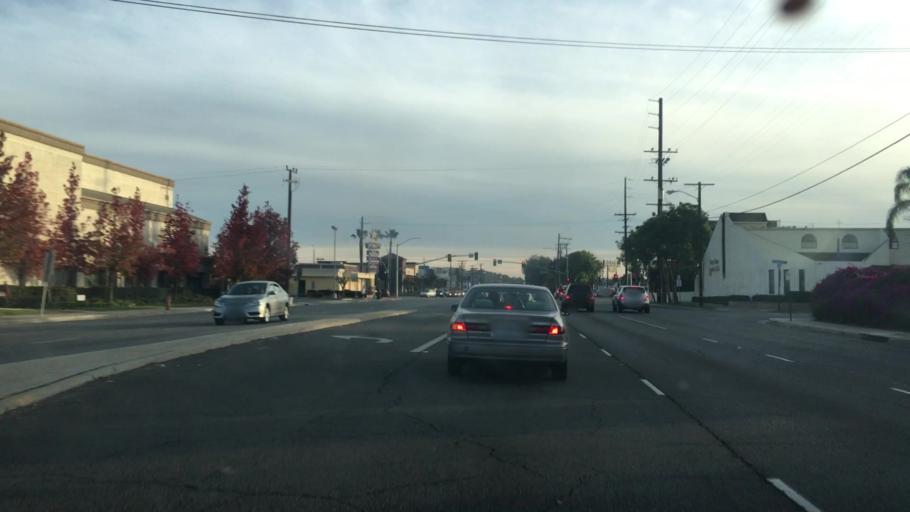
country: US
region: California
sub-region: Los Angeles County
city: Signal Hill
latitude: 33.8340
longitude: -118.1676
